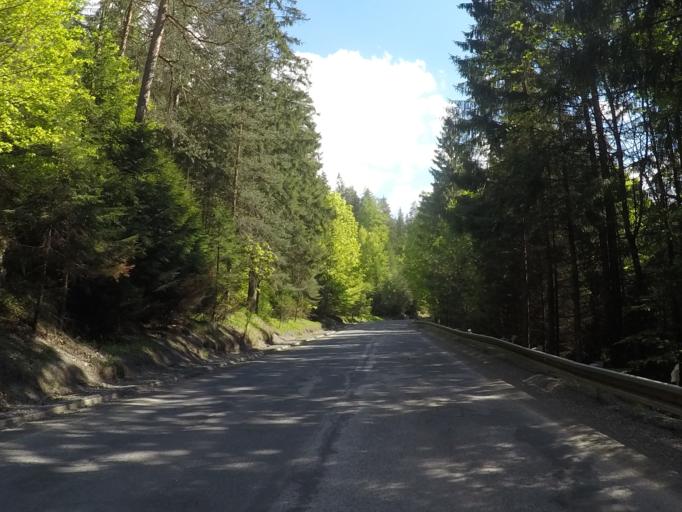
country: SK
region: Kosicky
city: Dobsina
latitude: 48.9140
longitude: 20.2609
